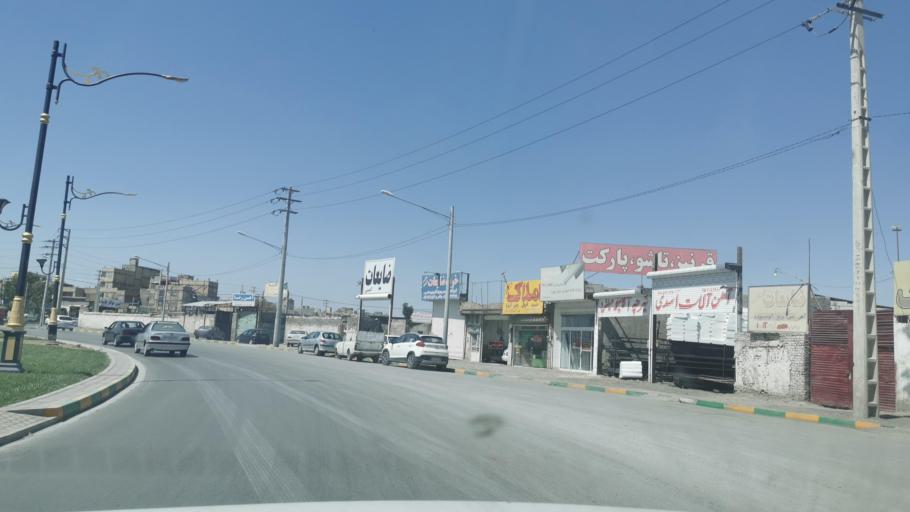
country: IR
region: Razavi Khorasan
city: Mashhad
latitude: 36.3542
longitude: 59.5711
